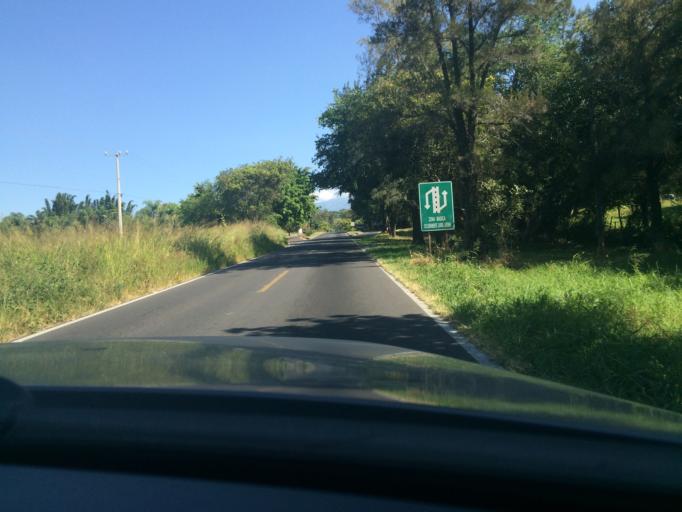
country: MX
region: Colima
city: Suchitlan
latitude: 19.3582
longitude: -103.7255
